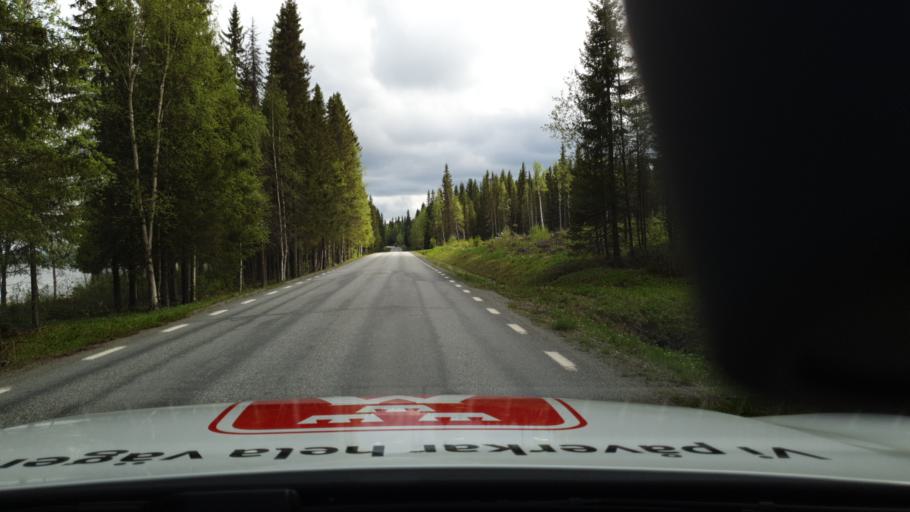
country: SE
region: Vaesterbotten
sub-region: Vilhelmina Kommun
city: Sjoberg
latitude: 64.6627
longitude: 16.3095
